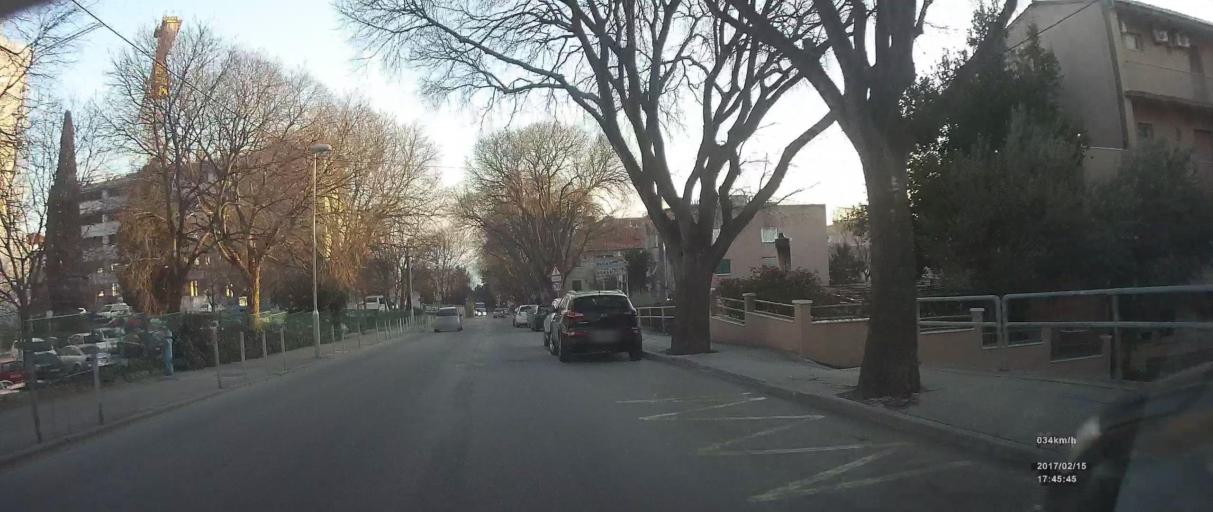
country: HR
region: Splitsko-Dalmatinska
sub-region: Grad Split
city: Split
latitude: 43.5036
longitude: 16.4567
